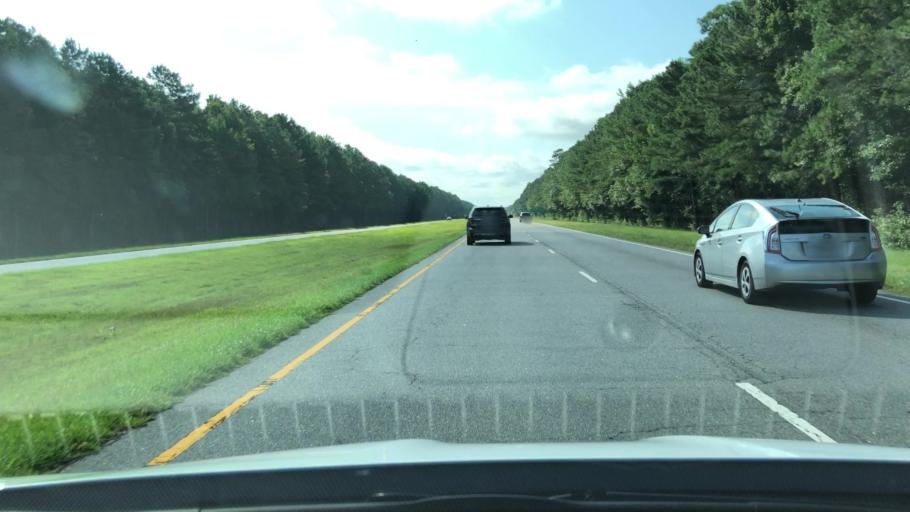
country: US
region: North Carolina
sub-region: Pasquotank County
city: Elizabeth City
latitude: 36.3925
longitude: -76.3240
